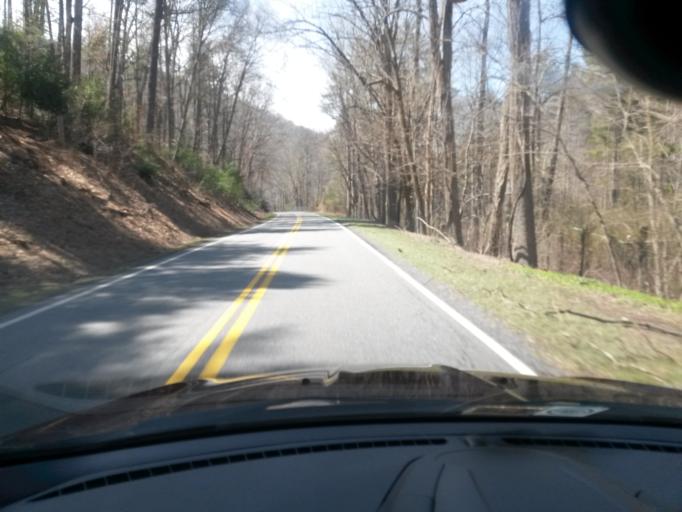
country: US
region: Virginia
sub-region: City of Covington
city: Covington
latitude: 37.7569
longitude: -80.1294
